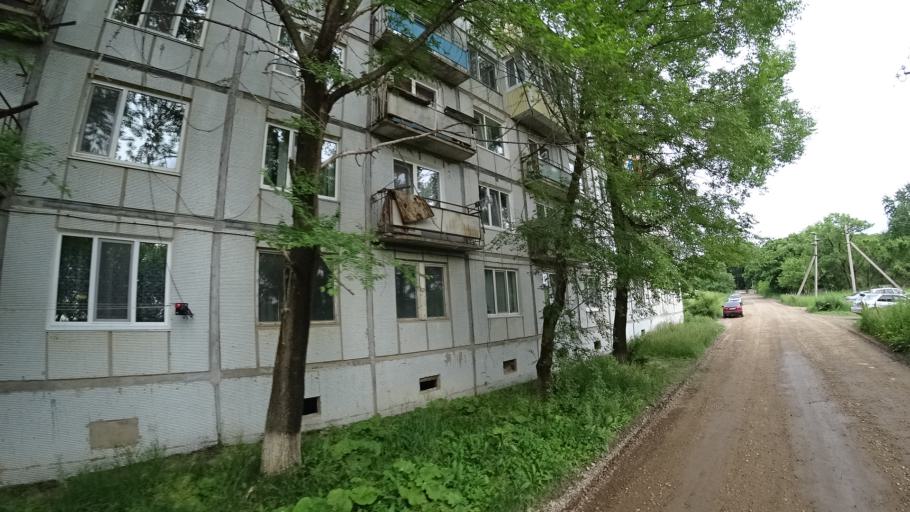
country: RU
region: Primorskiy
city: Novosysoyevka
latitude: 44.2272
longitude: 133.3568
